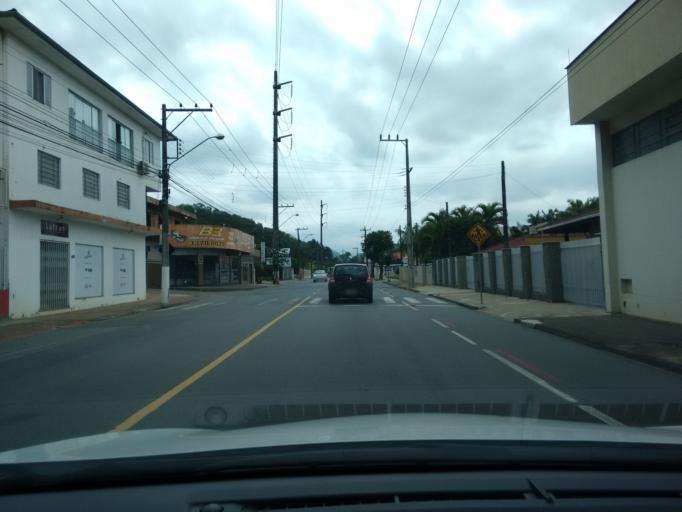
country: BR
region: Santa Catarina
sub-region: Jaragua Do Sul
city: Jaragua do Sul
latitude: -26.5073
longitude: -49.0993
